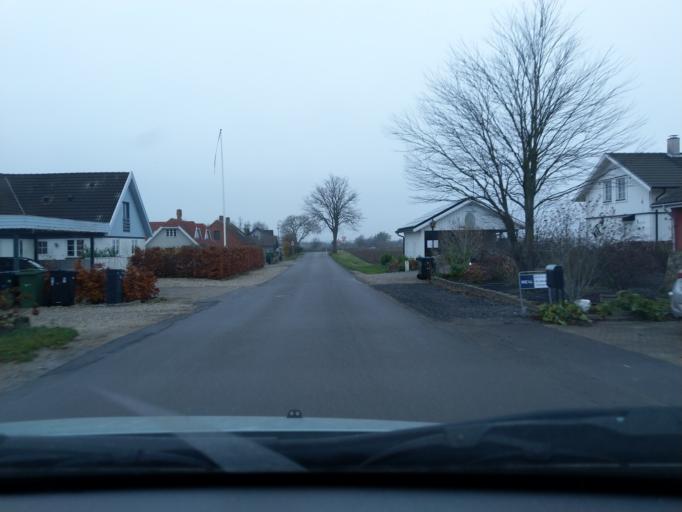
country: DK
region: Zealand
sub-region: Vordingborg Kommune
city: Praesto
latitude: 55.1086
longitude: 12.0700
